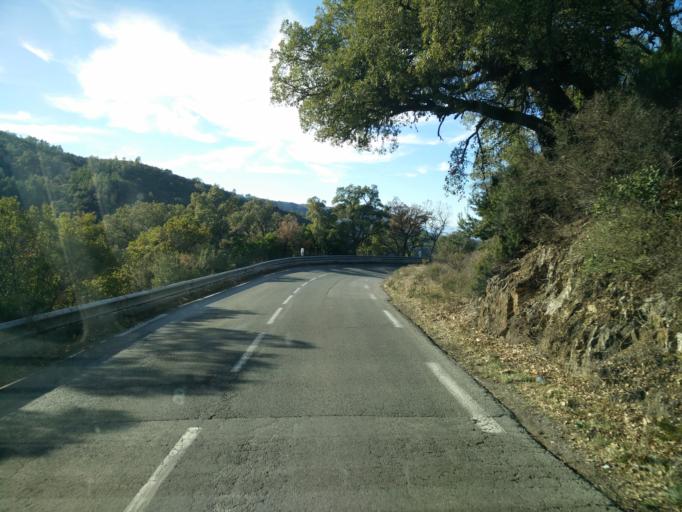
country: FR
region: Provence-Alpes-Cote d'Azur
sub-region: Departement du Var
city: La Garde-Freinet
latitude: 43.3305
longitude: 6.4587
